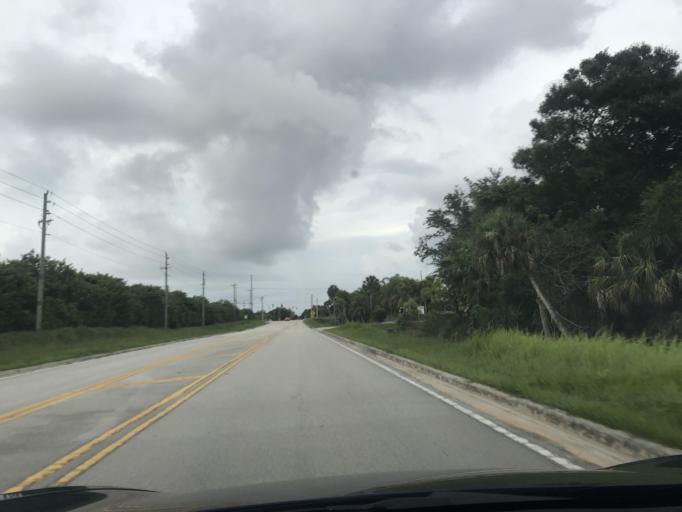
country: US
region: Florida
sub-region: Indian River County
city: Vero Beach South
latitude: 27.6167
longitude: -80.4498
